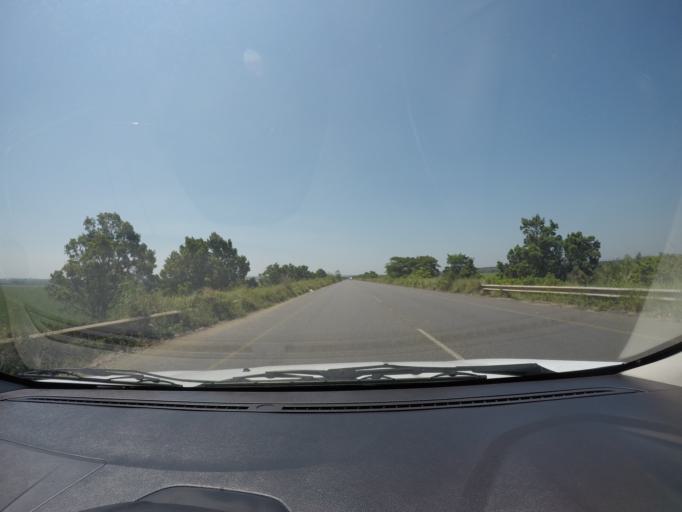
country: ZA
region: KwaZulu-Natal
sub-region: uThungulu District Municipality
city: Empangeni
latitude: -28.7893
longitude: 31.9581
